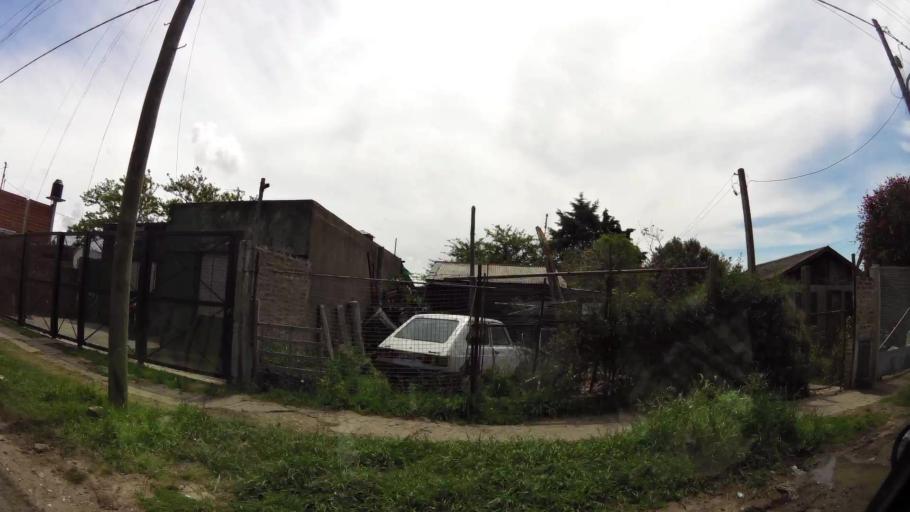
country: AR
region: Buenos Aires
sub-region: Partido de Quilmes
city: Quilmes
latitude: -34.7827
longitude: -58.2749
